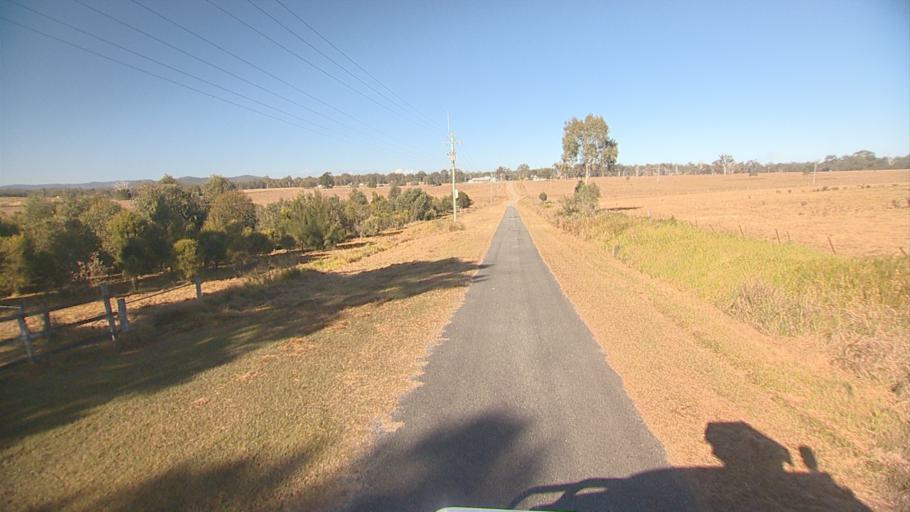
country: AU
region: Queensland
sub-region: Logan
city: North Maclean
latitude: -27.7653
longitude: 153.0473
